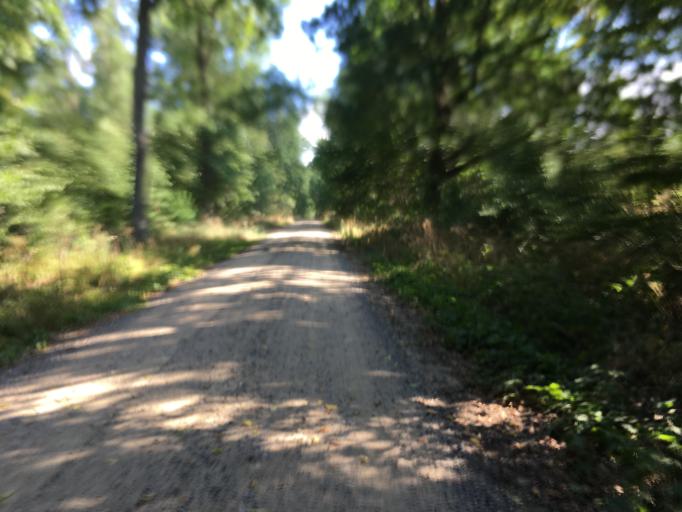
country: DE
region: Brandenburg
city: Liebenwalde
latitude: 52.9201
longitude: 13.4337
